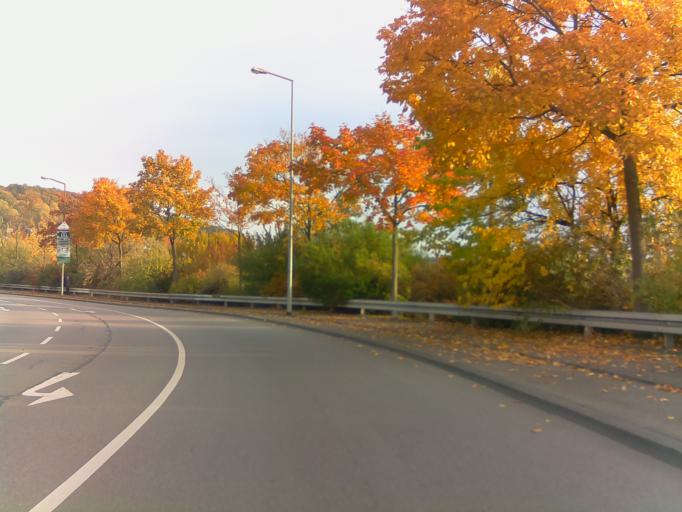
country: DE
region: Baden-Wuerttemberg
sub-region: Karlsruhe Region
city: Weinheim
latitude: 49.5400
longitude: 8.6560
